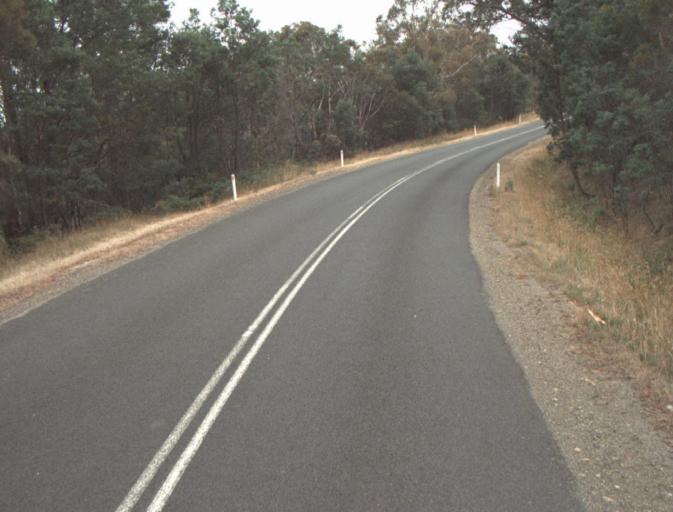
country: AU
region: Tasmania
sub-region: Northern Midlands
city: Evandale
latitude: -41.5054
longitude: 147.3805
